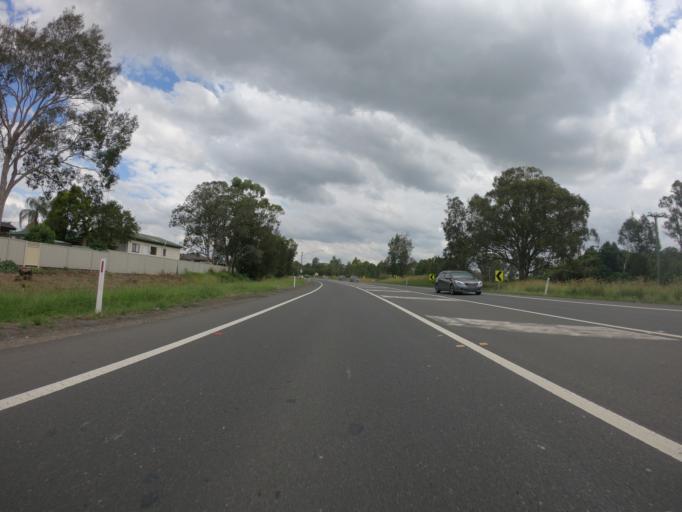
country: AU
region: New South Wales
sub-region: Blacktown
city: Mount Druitt
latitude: -33.8013
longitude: 150.7683
